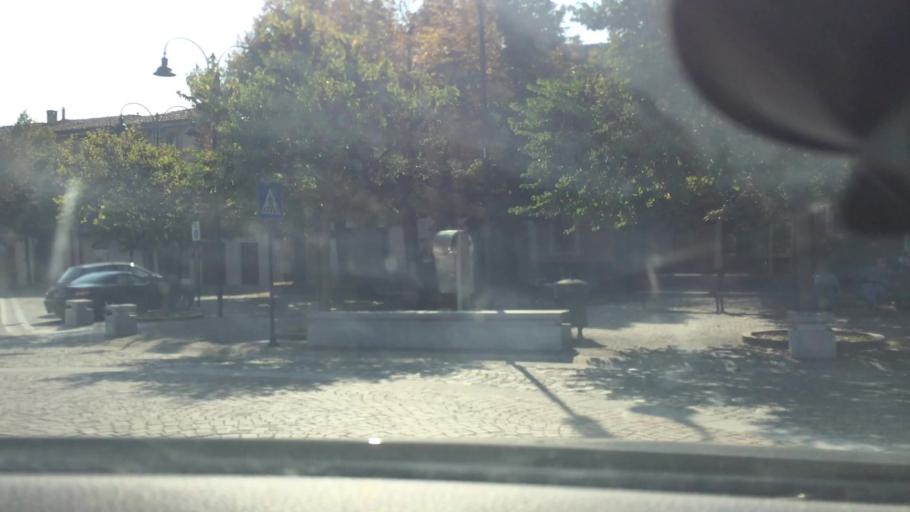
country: IT
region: Lombardy
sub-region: Citta metropolitana di Milano
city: Busto Garolfo
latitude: 45.5456
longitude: 8.8832
